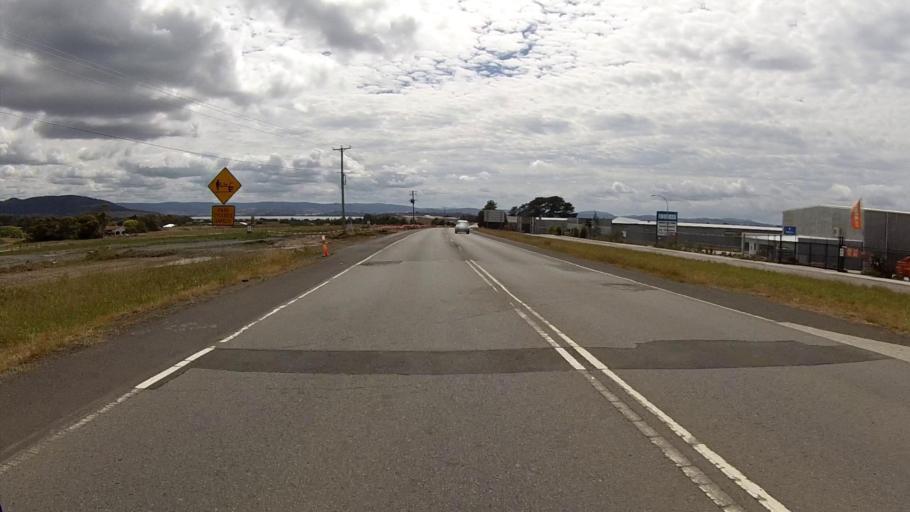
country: AU
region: Tasmania
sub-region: Clarence
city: Cambridge
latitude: -42.8334
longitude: 147.4569
